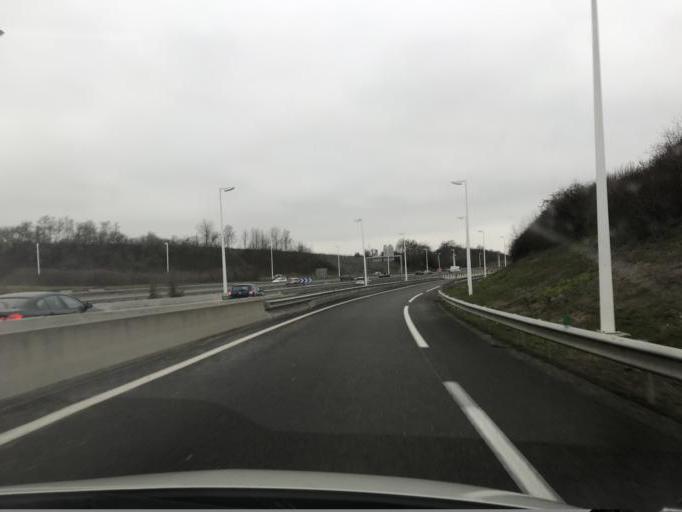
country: FR
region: Rhone-Alpes
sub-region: Departement de la Haute-Savoie
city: Neydens
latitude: 46.1336
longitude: 6.0976
